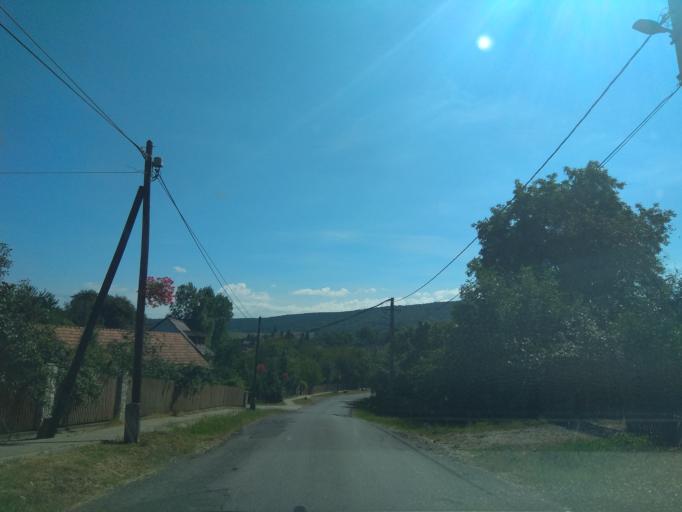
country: HU
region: Borsod-Abauj-Zemplen
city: Sajokaza
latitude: 48.1704
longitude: 20.5272
